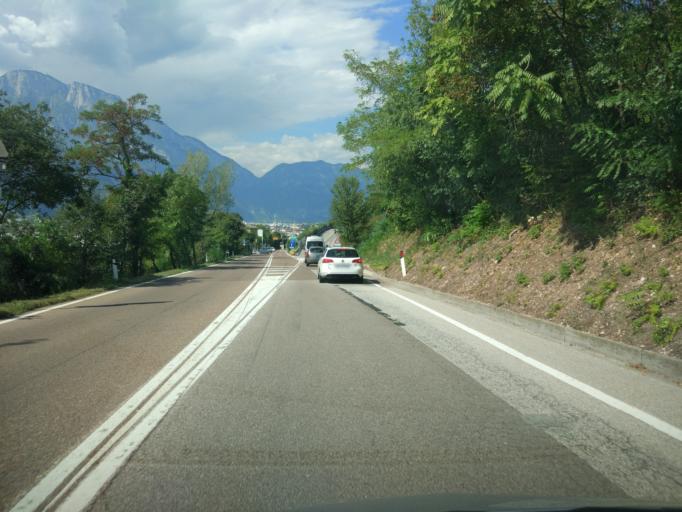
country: IT
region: Trentino-Alto Adige
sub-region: Provincia di Trento
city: Trento
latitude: 46.0880
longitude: 11.1247
